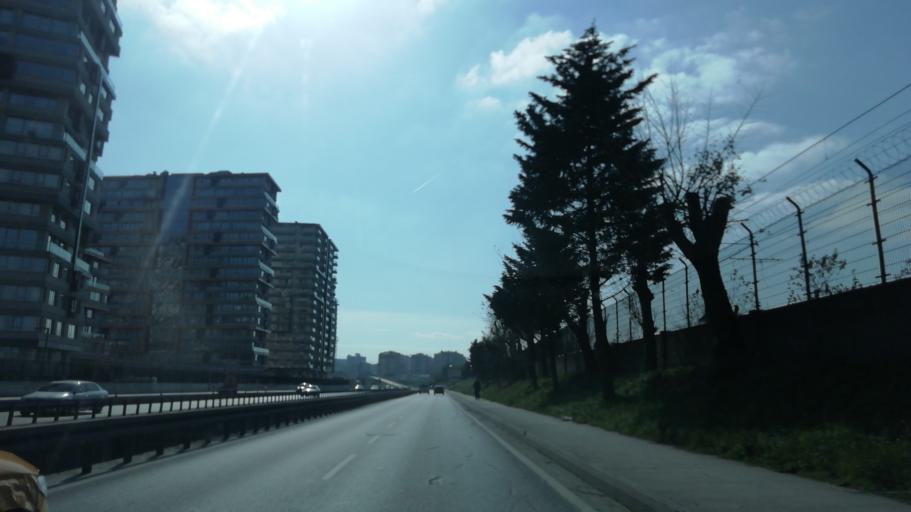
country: TR
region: Istanbul
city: merter keresteciler
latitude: 41.0266
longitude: 28.8991
